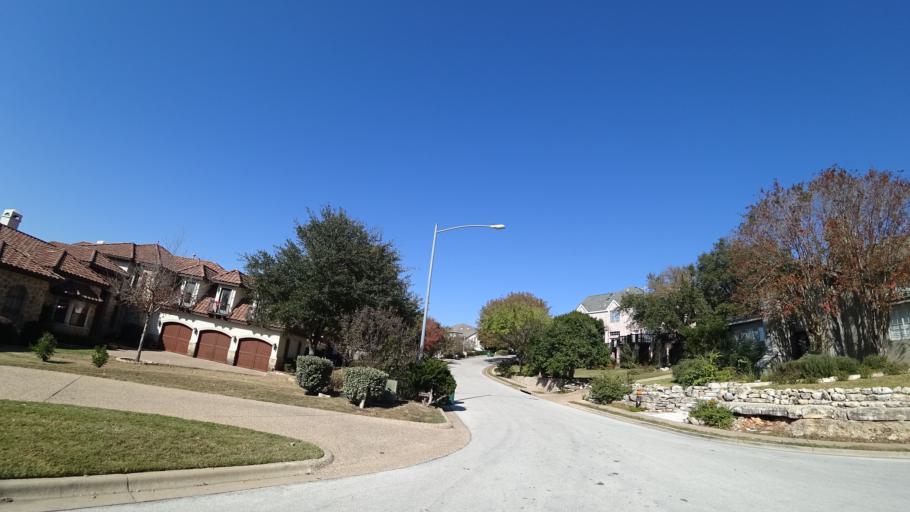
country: US
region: Texas
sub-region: Travis County
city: Lost Creek
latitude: 30.3660
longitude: -97.8630
